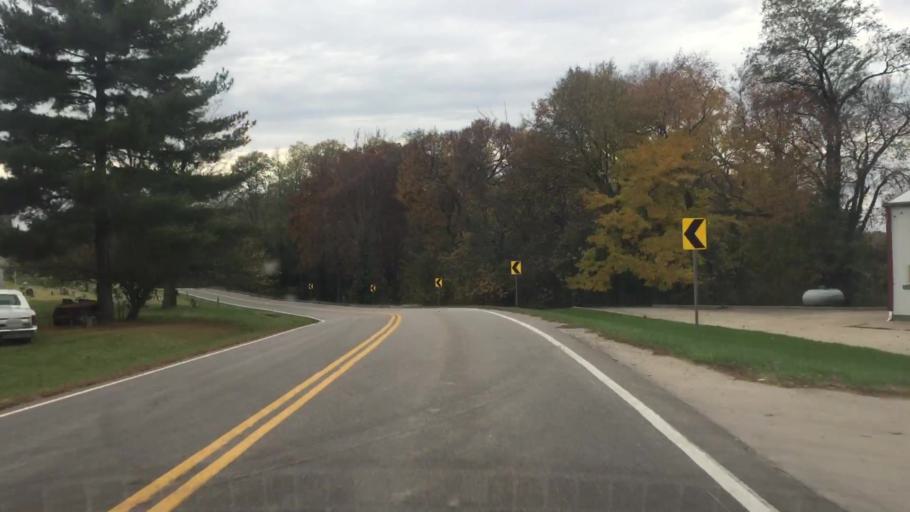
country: US
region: Missouri
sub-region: Osage County
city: Linn
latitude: 38.7139
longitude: -91.7137
